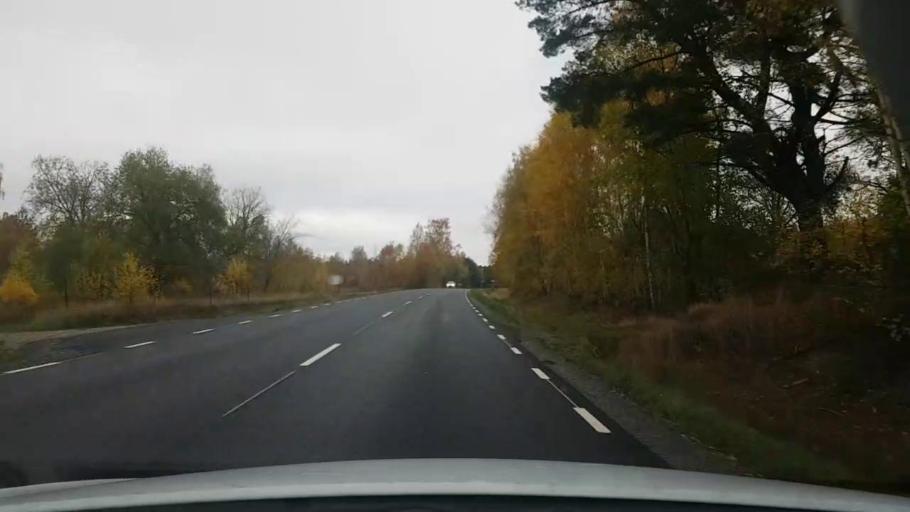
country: SE
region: OErebro
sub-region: Laxa Kommun
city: Laxa
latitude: 58.8088
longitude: 14.5455
